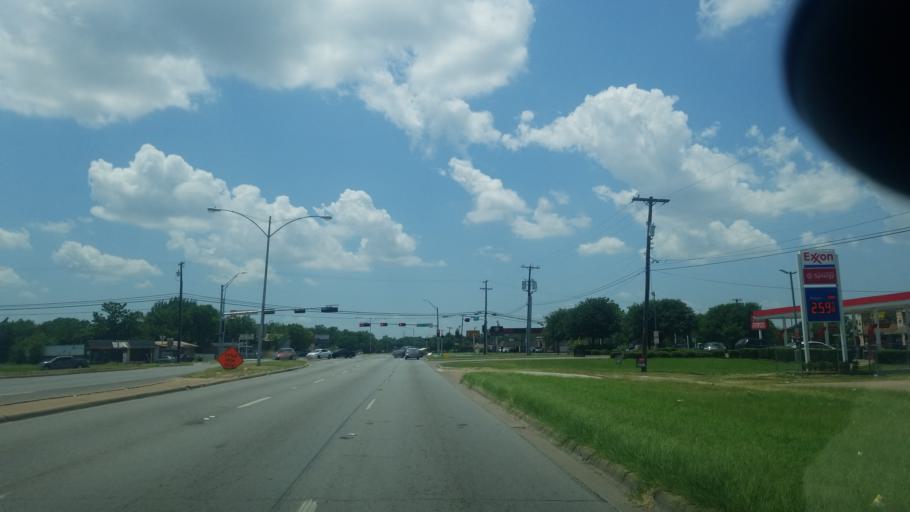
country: US
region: Texas
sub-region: Dallas County
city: Dallas
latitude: 32.7165
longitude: -96.7757
